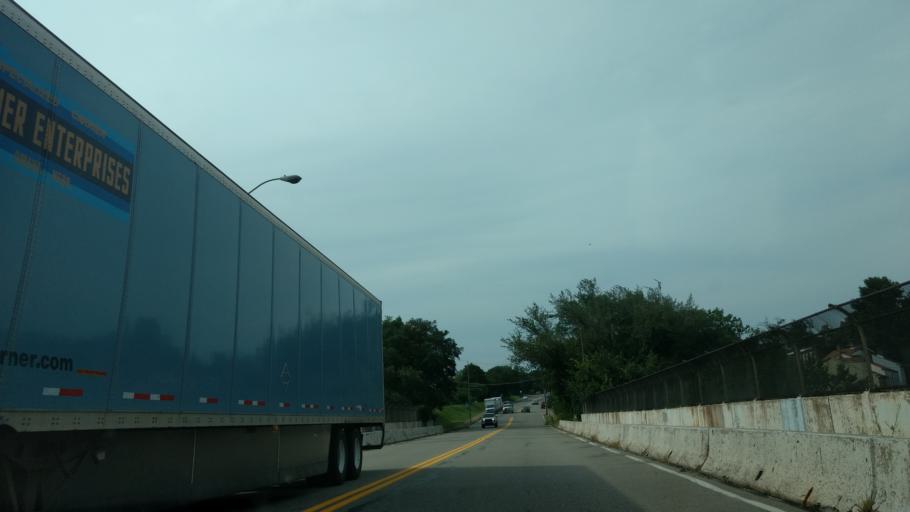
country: US
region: Pennsylvania
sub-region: Allegheny County
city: Bellevue
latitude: 40.4718
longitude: -80.0370
